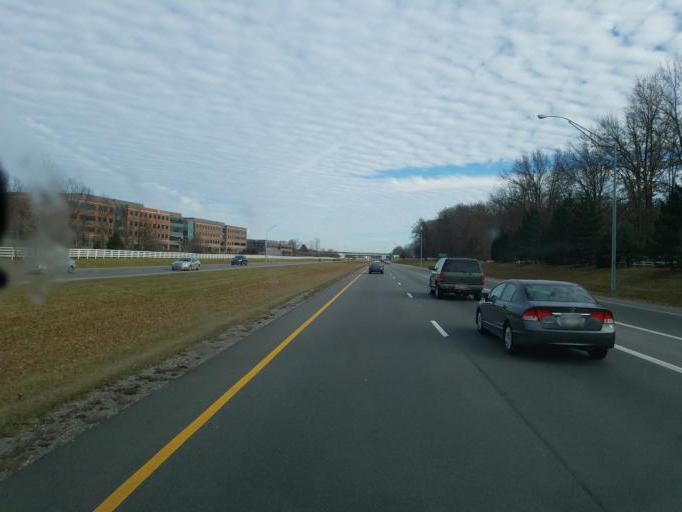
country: US
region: Ohio
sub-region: Franklin County
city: New Albany
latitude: 40.0911
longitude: -82.8185
